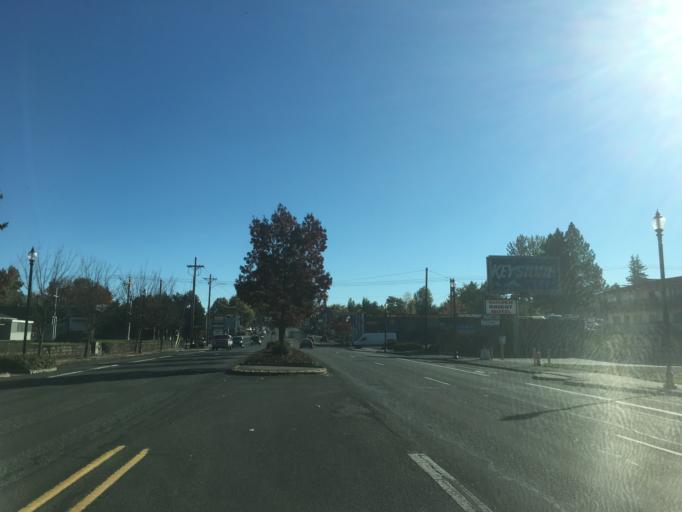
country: US
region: Oregon
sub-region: Multnomah County
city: Gresham
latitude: 45.4981
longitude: -122.4240
